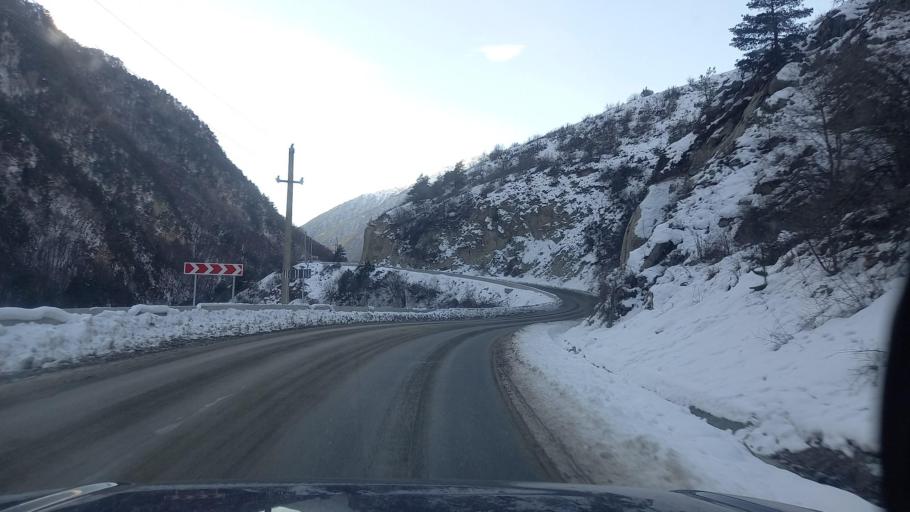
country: RU
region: North Ossetia
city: Chikola
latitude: 42.9756
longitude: 43.7620
